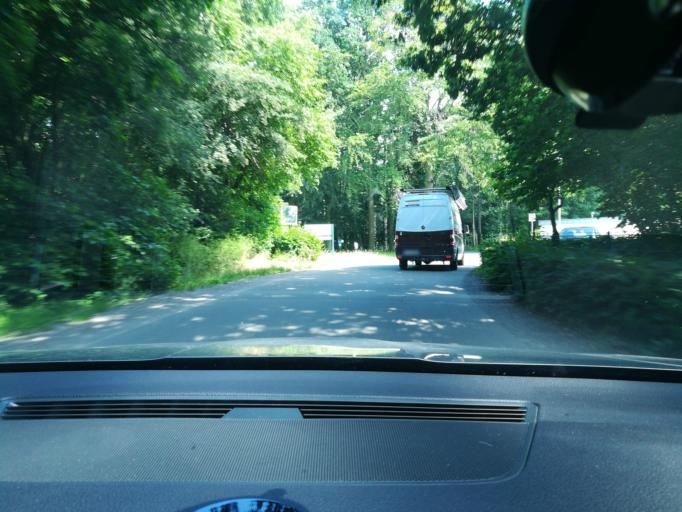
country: DE
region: North Rhine-Westphalia
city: Lubbecke
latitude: 52.3331
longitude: 8.6268
